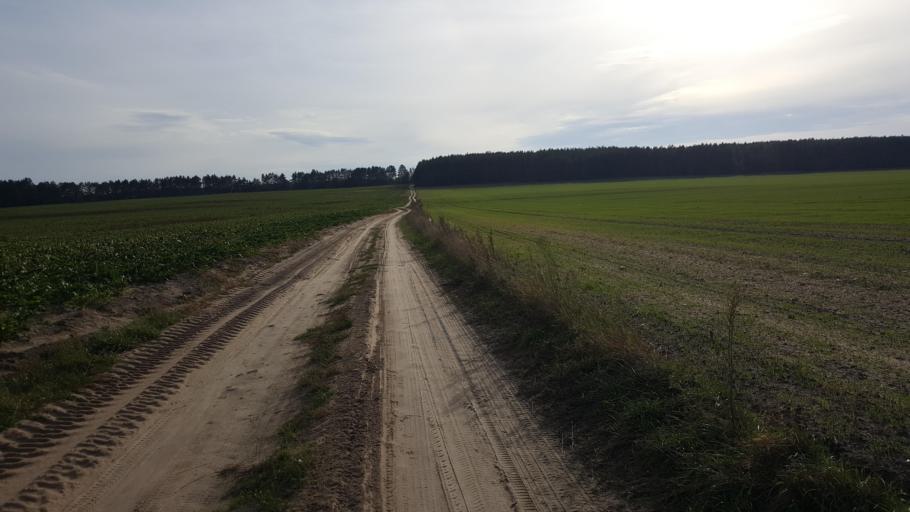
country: BY
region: Brest
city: Kamyanyets
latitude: 52.3929
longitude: 23.8512
